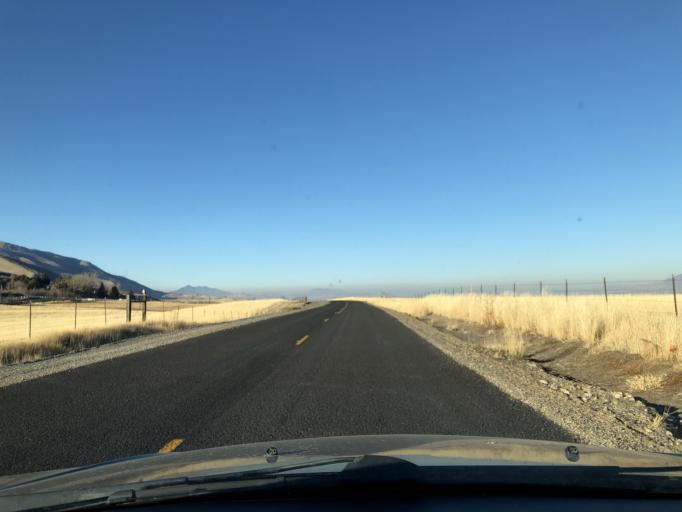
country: US
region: Utah
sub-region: Cache County
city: Wellsville
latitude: 41.5913
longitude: -111.9268
